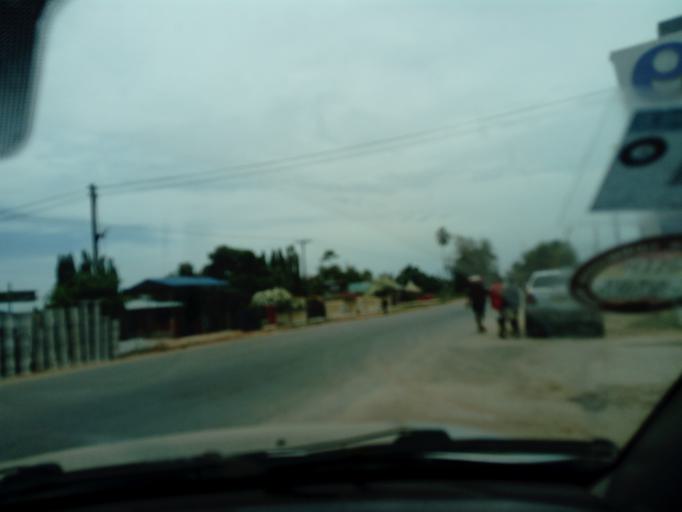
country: GH
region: Central
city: Cape Coast
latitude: 5.1386
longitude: -1.2809
